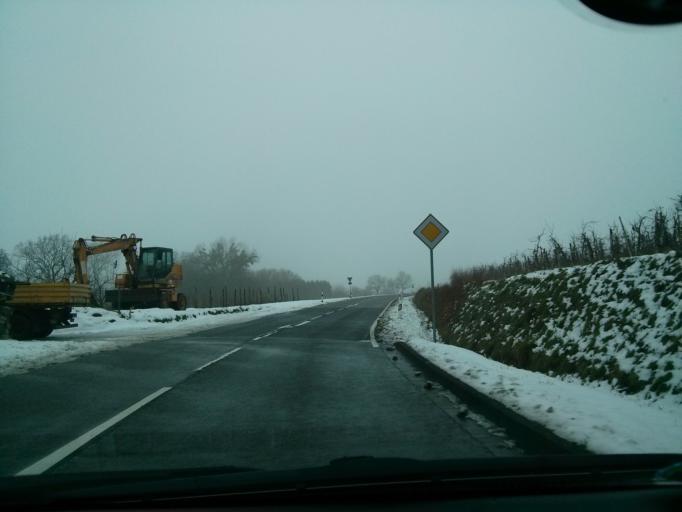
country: DE
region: Rheinland-Pfalz
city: Kalenborn
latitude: 50.5874
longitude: 7.0082
